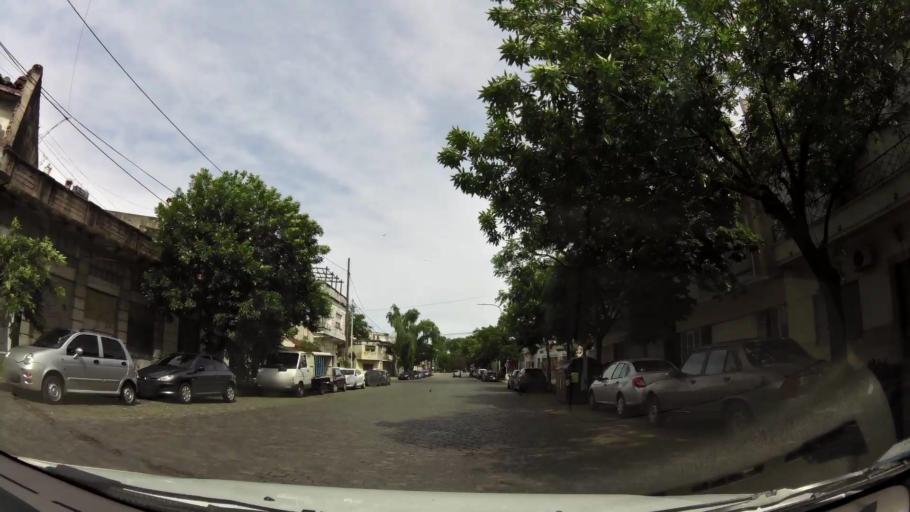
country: AR
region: Buenos Aires F.D.
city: Villa Santa Rita
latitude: -34.6344
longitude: -58.4967
